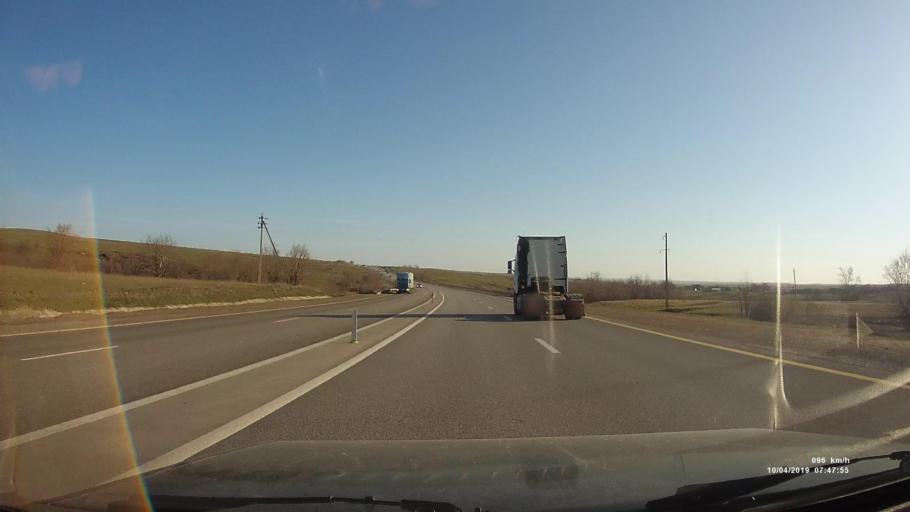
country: RU
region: Rostov
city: Kamensk-Shakhtinskiy
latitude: 48.2265
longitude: 40.2768
